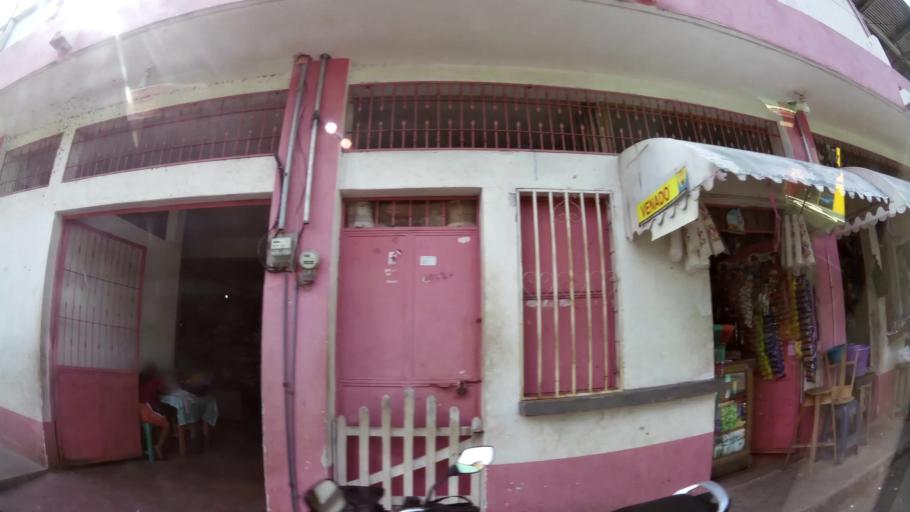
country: GT
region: Suchitepeque
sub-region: Municipio de Cuyotenango
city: Cuyotenango
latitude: 14.5387
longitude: -91.5711
